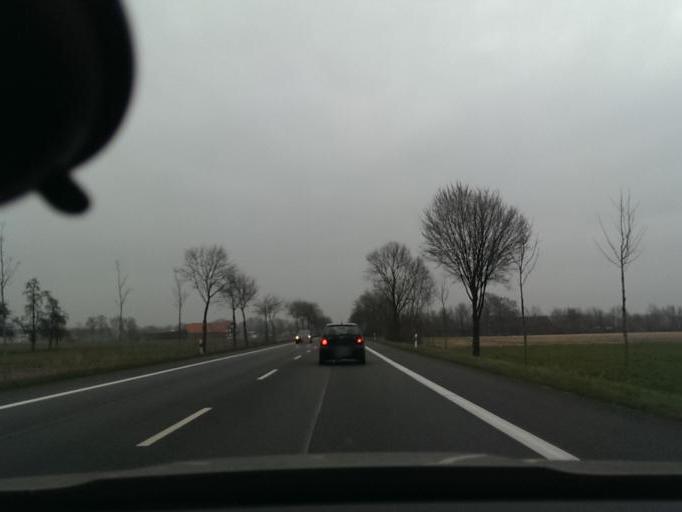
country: DE
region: North Rhine-Westphalia
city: Rietberg
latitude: 51.7798
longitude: 8.4878
